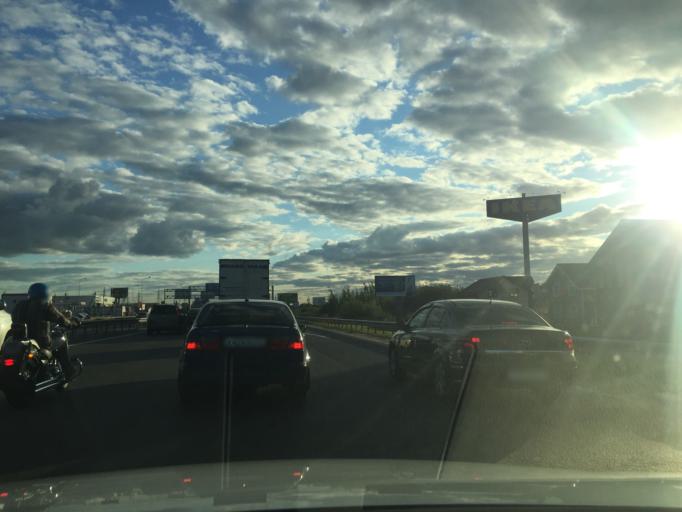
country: RU
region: Leningrad
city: Rybatskoye
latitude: 59.8905
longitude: 30.5170
